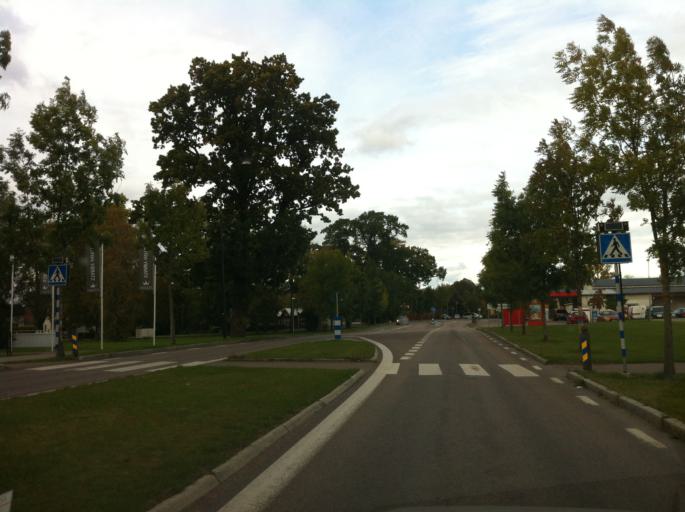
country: SE
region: OEstergoetland
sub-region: Vadstena Kommun
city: Vadstena
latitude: 58.4353
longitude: 14.8772
